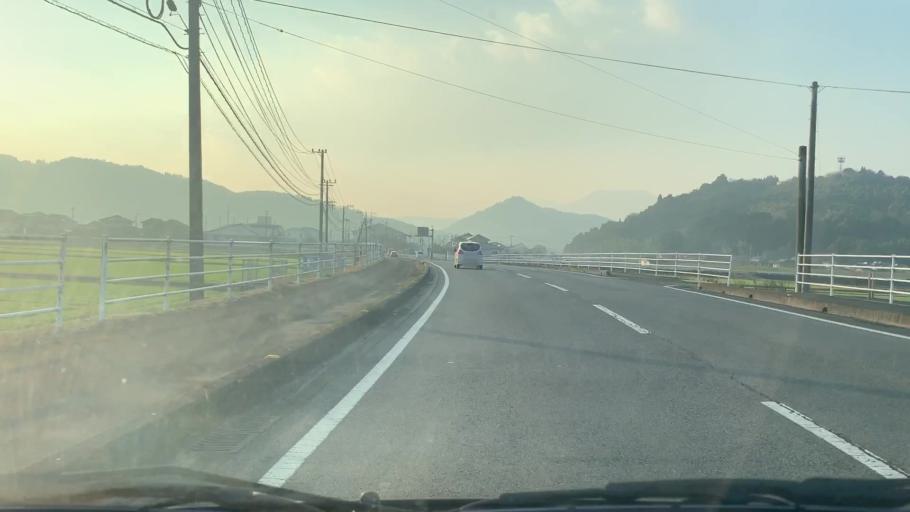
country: JP
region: Saga Prefecture
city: Takeocho-takeo
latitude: 33.2723
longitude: 130.1303
